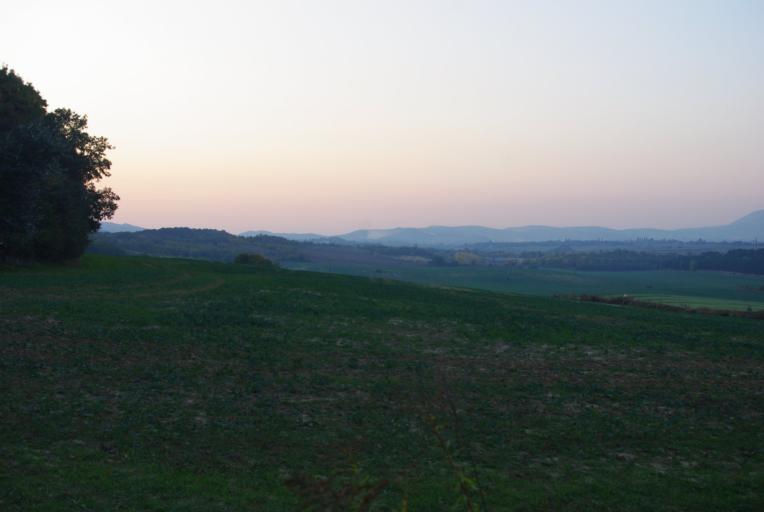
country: HU
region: Pest
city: Pilisborosjeno
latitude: 47.5803
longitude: 18.9766
